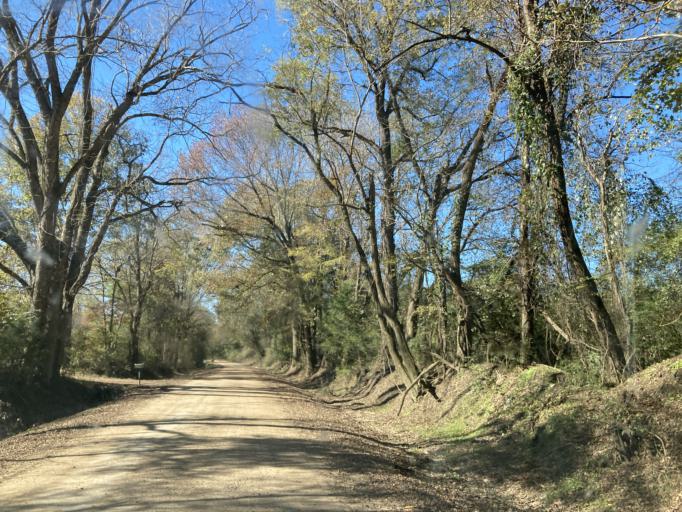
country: US
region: Mississippi
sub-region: Hinds County
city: Lynchburg
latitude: 32.5822
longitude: -90.5718
